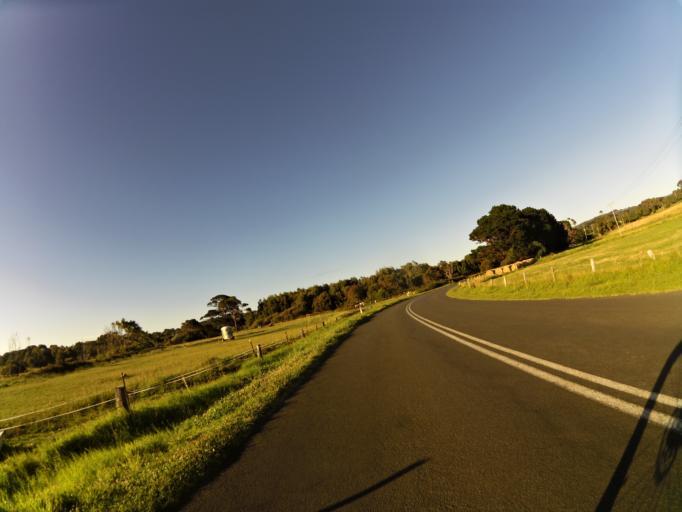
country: AU
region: Victoria
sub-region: Colac-Otway
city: Apollo Bay
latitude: -38.7669
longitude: 143.6582
